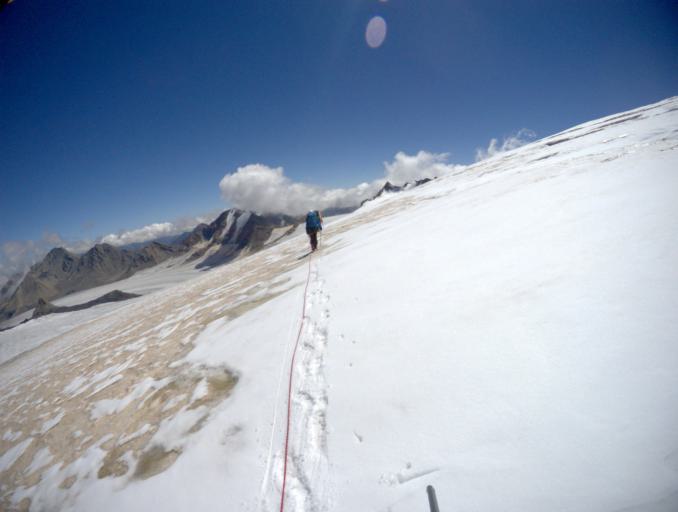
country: RU
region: Kabardino-Balkariya
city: Terskol
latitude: 43.3544
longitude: 42.5032
